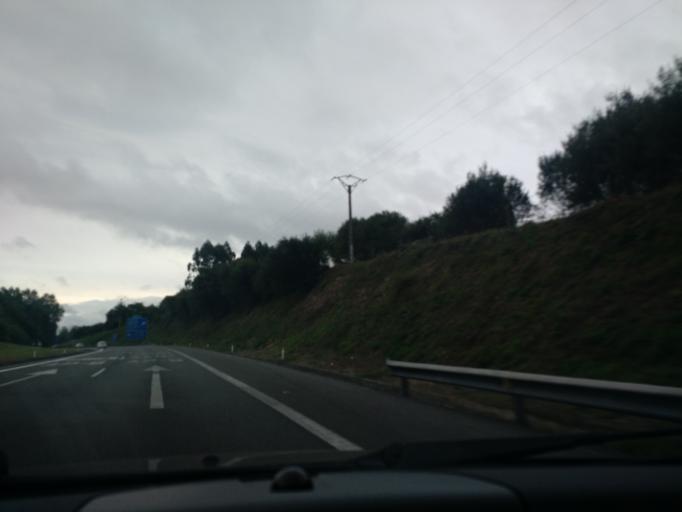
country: ES
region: Galicia
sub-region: Provincia da Coruna
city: Oleiros
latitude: 43.2910
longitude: -8.2959
